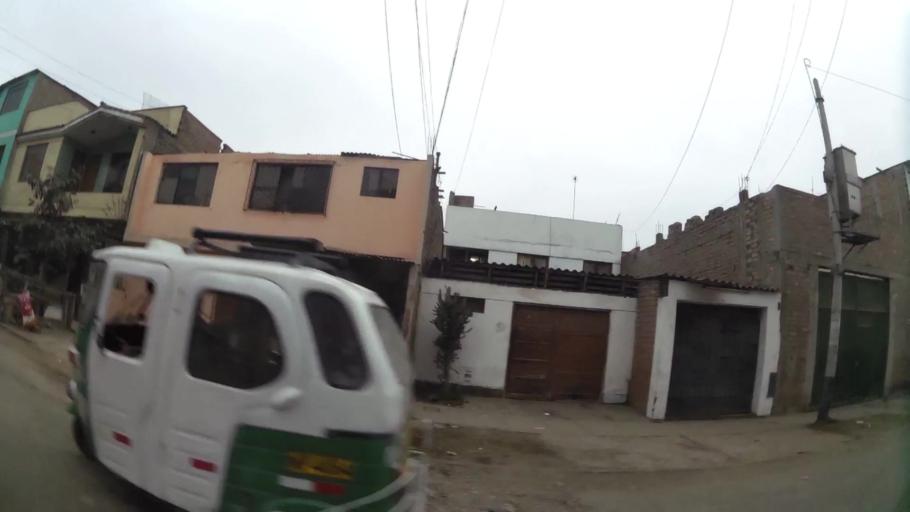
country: PE
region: Lima
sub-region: Lima
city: Surco
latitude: -12.1473
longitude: -76.9762
